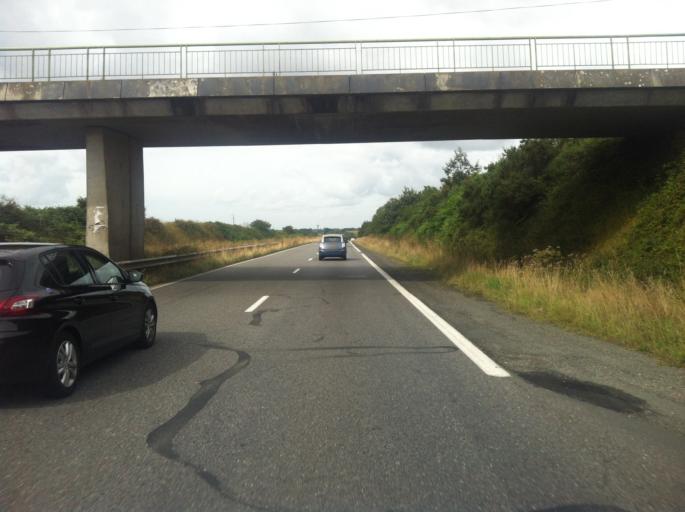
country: FR
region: Brittany
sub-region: Departement du Finistere
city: La Roche-Maurice
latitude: 48.4951
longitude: -4.2029
